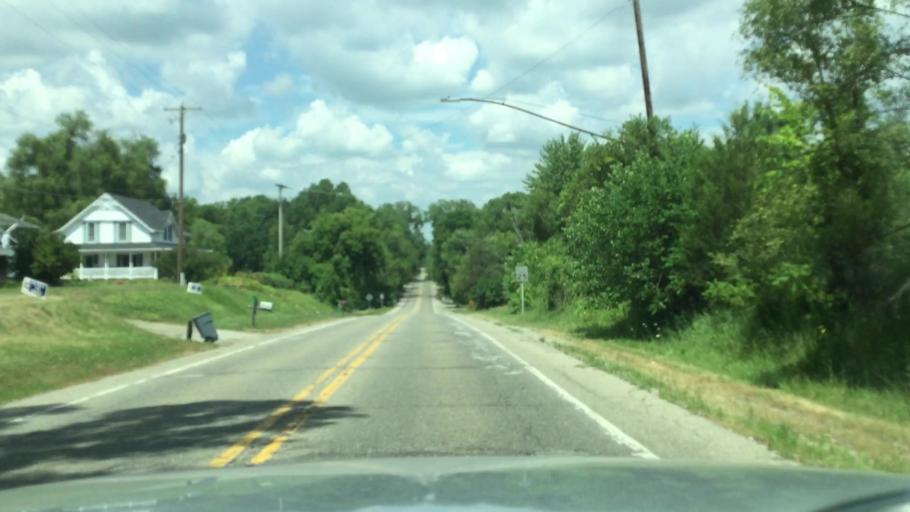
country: US
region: Michigan
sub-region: Genesee County
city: Flushing
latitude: 43.0641
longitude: -83.8635
